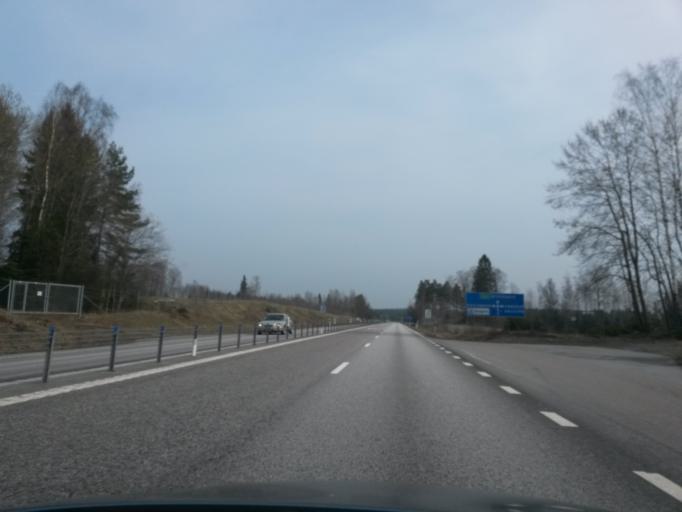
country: SE
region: Vaestra Goetaland
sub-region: Gullspangs Kommun
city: Anderstorp
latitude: 58.8997
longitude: 14.3361
